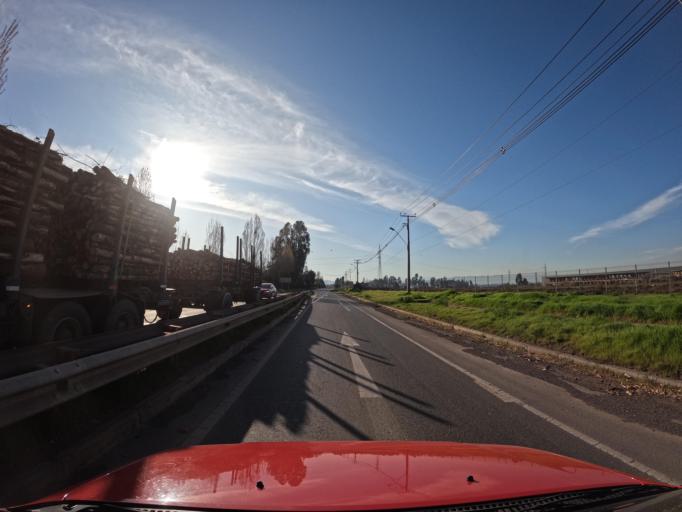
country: CL
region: Maule
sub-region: Provincia de Curico
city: Teno
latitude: -34.8647
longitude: -71.0920
